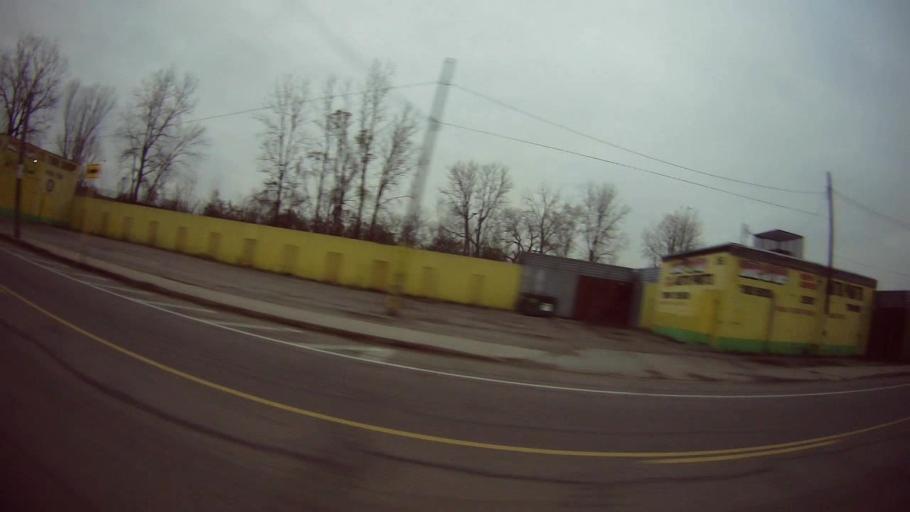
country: US
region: Michigan
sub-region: Wayne County
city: Highland Park
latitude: 42.4186
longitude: -83.0763
